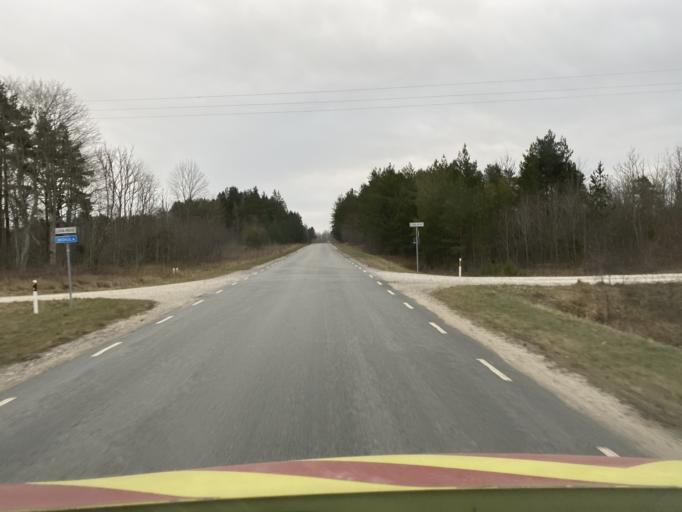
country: EE
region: Laeaene
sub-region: Ridala Parish
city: Uuemoisa
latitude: 59.0358
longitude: 23.6370
